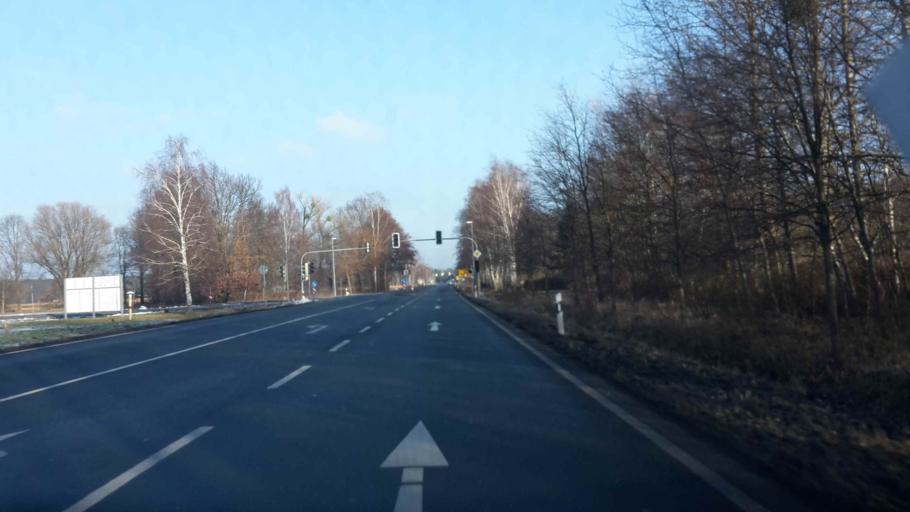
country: DE
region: Brandenburg
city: Wittenberge
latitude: 53.0165
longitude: 11.7361
